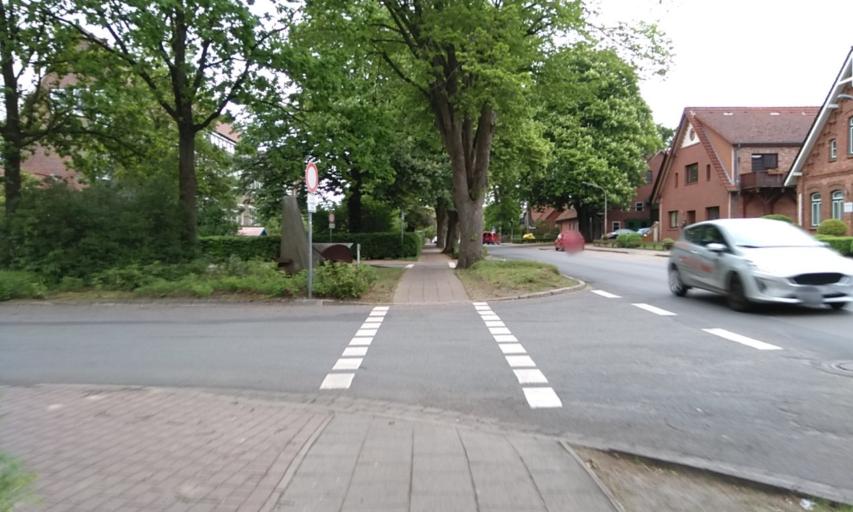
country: DE
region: Lower Saxony
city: Harsefeld
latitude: 53.4526
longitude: 9.4946
